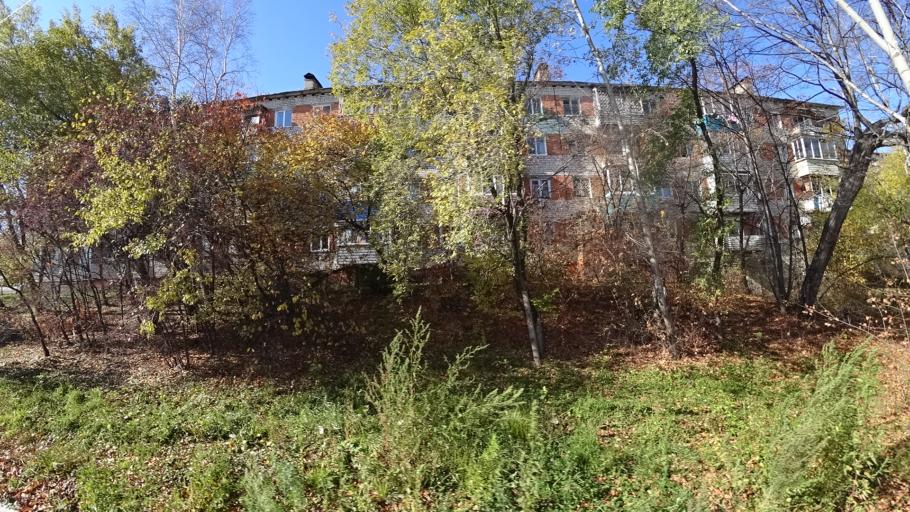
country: RU
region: Khabarovsk Krai
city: Amursk
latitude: 50.2156
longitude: 136.9062
